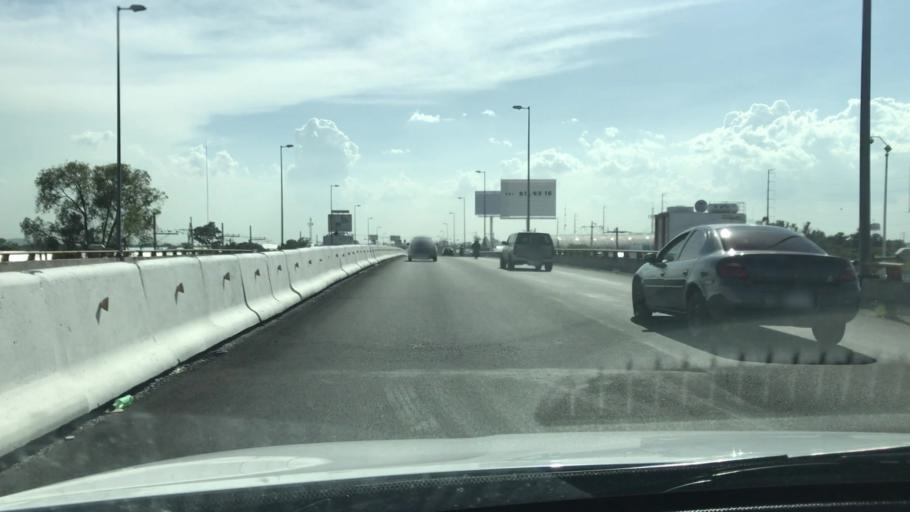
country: MX
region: Guanajuato
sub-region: Celaya
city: Colonia Pedro Maria Anaya
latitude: 20.5186
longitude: -100.8488
